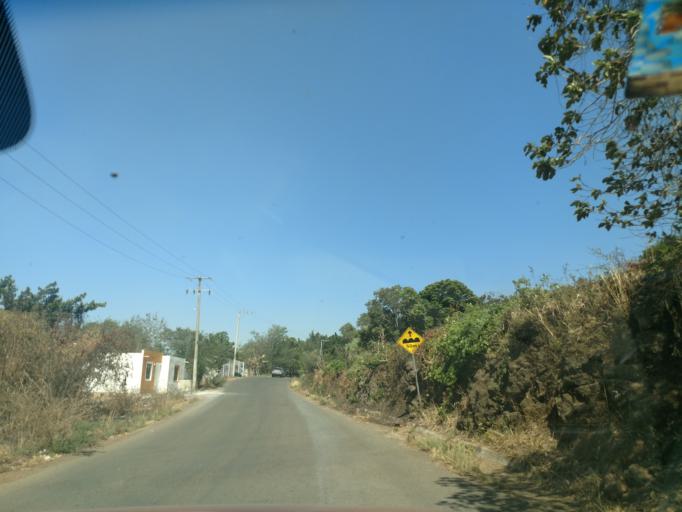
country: MX
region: Nayarit
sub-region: Tepic
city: La Corregidora
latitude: 21.4721
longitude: -104.6669
